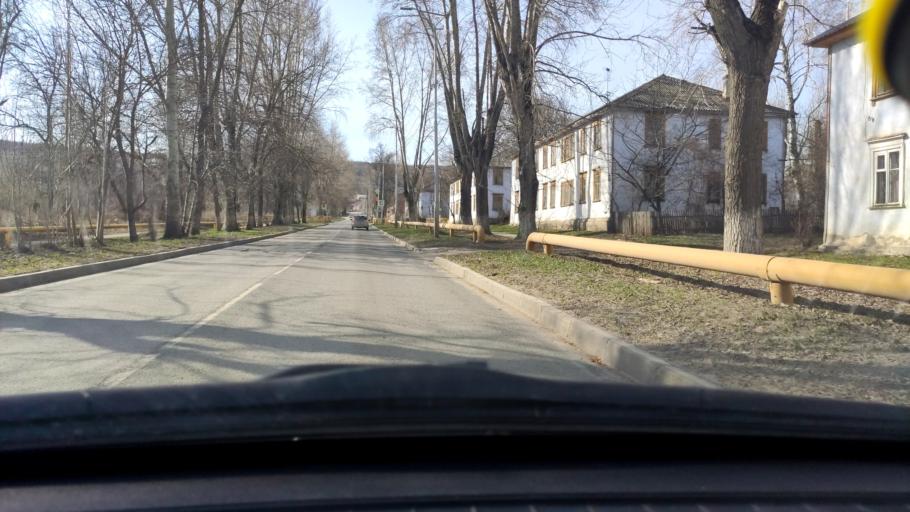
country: RU
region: Samara
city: Zhigulevsk
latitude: 53.3991
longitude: 49.4976
